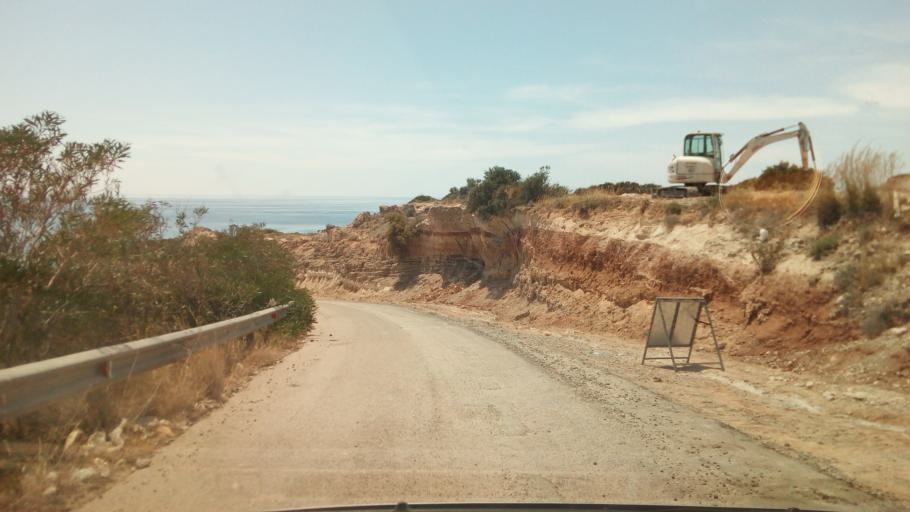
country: CY
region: Limassol
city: Pissouri
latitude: 34.6867
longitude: 32.5988
